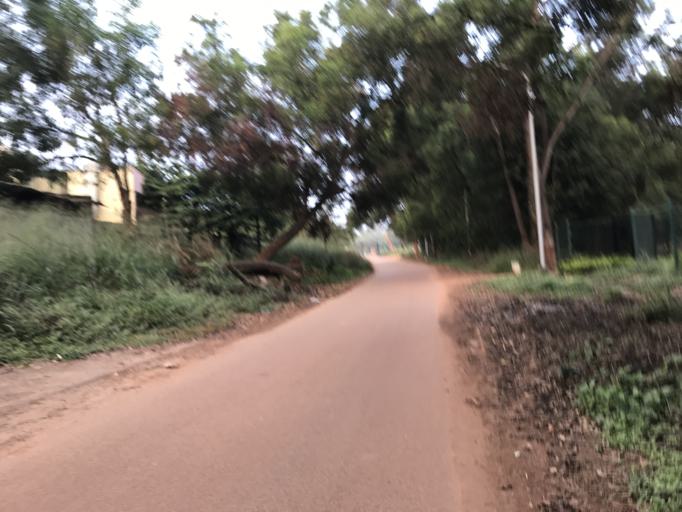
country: IN
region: Karnataka
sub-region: Bangalore Urban
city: Yelahanka
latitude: 13.0750
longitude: 77.5798
